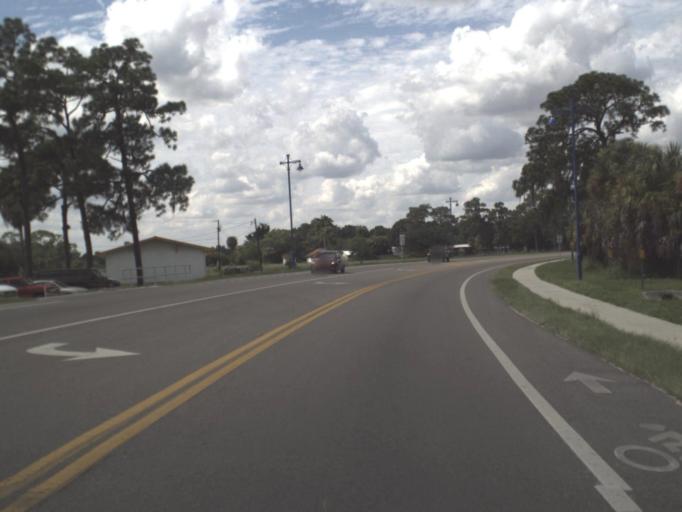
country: US
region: Florida
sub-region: Collier County
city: Immokalee
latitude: 26.4187
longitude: -81.4299
